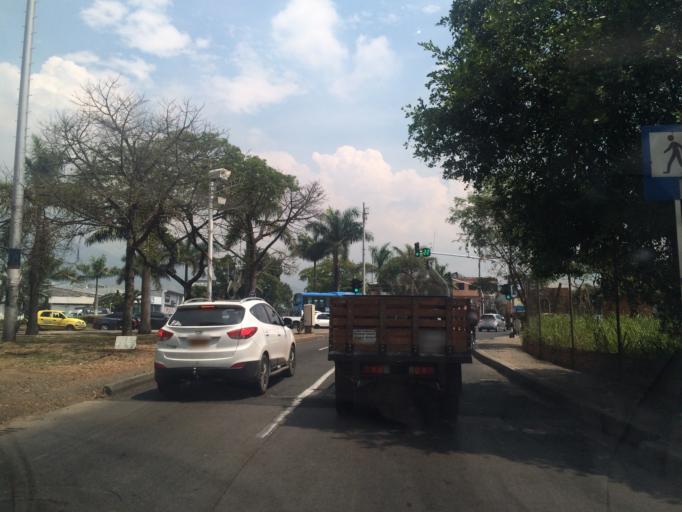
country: CO
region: Valle del Cauca
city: Cali
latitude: 3.4755
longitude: -76.5041
